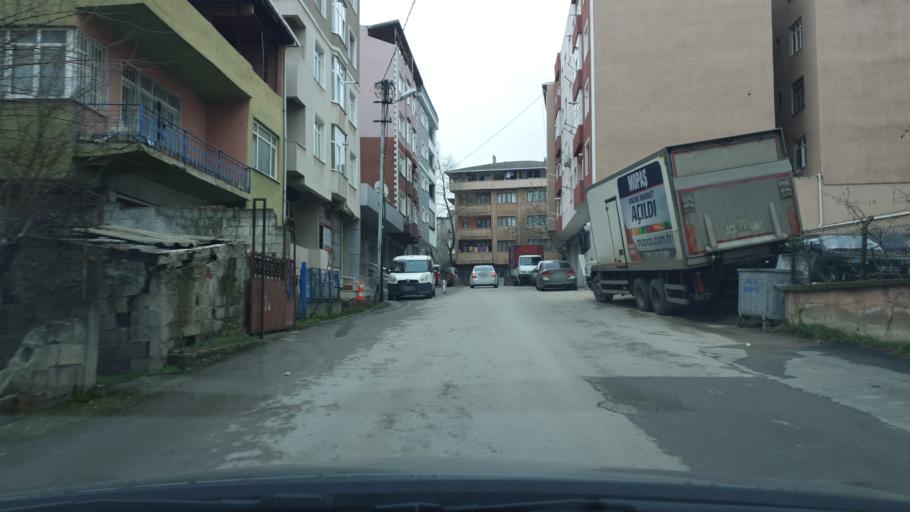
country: TR
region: Istanbul
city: Pendik
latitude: 40.8686
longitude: 29.2676
